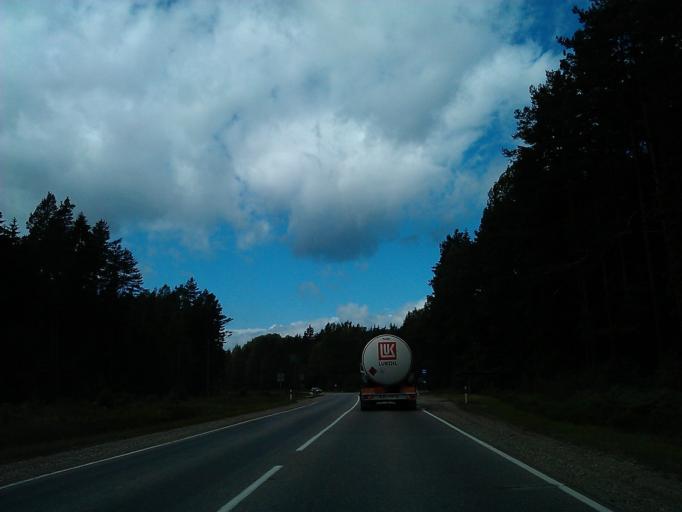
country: LV
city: Tireli
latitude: 56.9329
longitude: 23.4899
